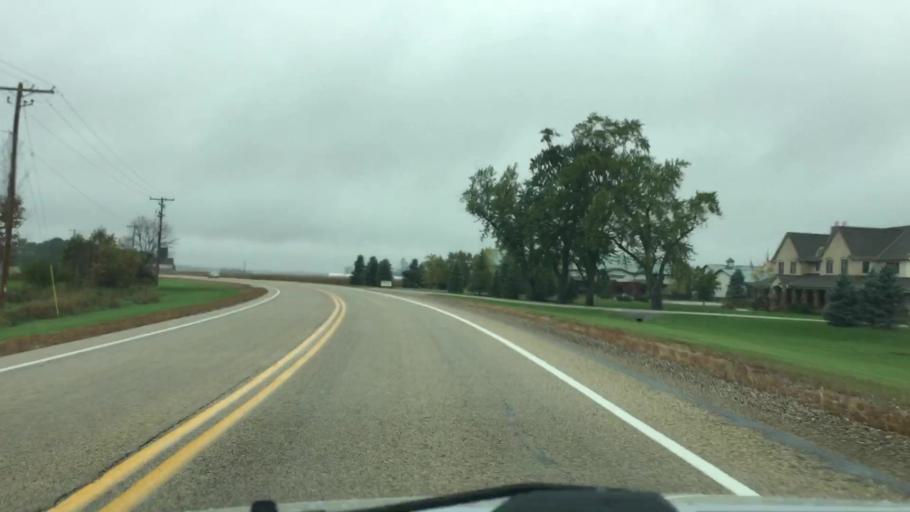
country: US
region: Wisconsin
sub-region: Jefferson County
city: Palmyra
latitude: 42.8809
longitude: -88.6235
